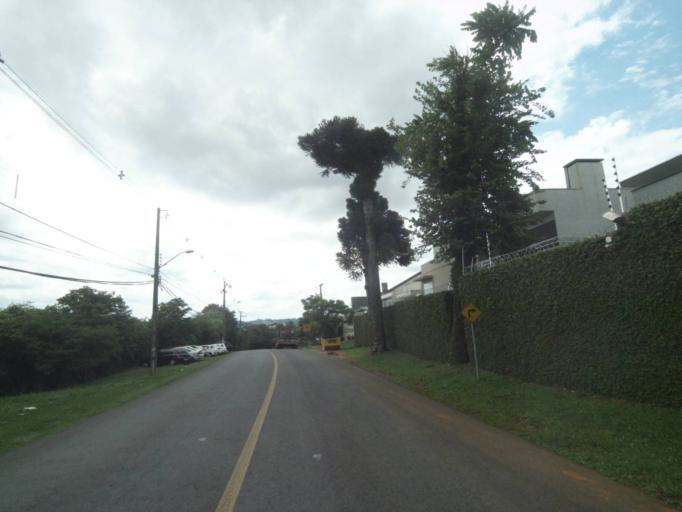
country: BR
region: Parana
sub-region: Curitiba
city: Curitiba
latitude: -25.3819
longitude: -49.2892
